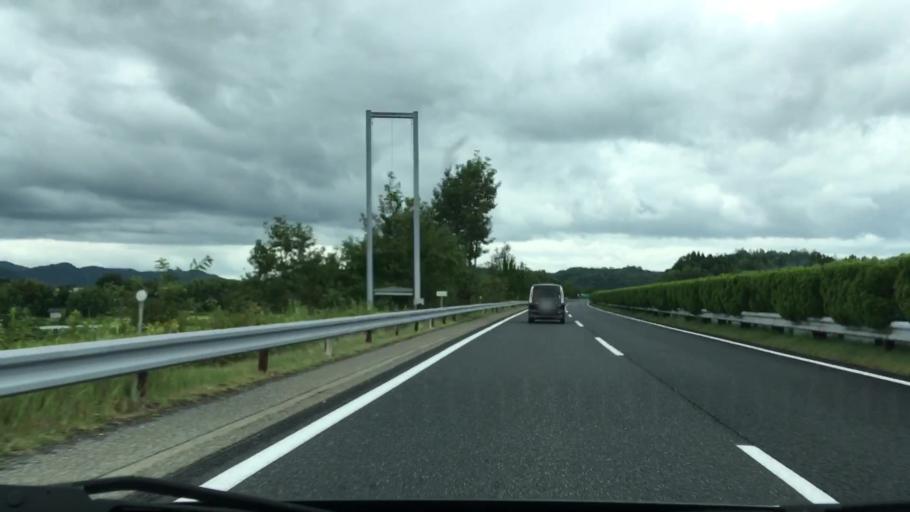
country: JP
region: Okayama
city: Tsuyama
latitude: 35.0465
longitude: 134.0748
